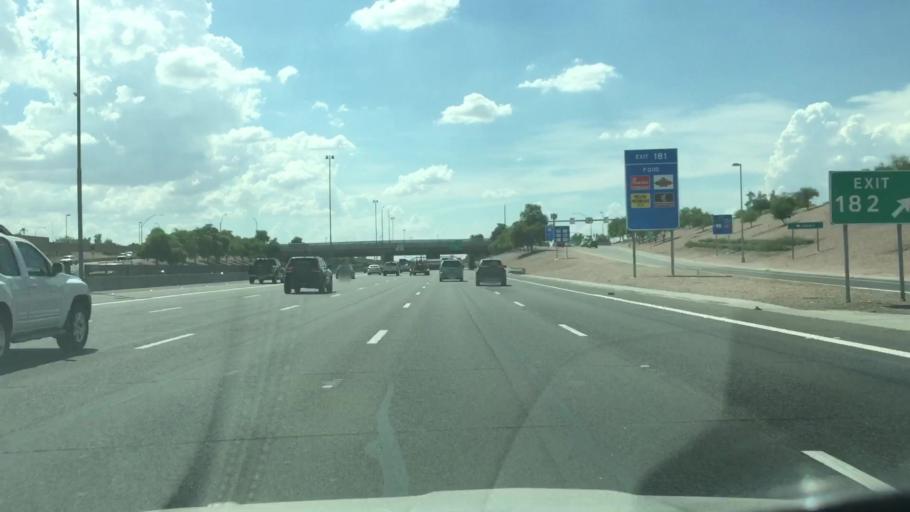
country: US
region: Arizona
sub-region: Maricopa County
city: Gilbert
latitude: 33.3848
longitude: -111.7851
